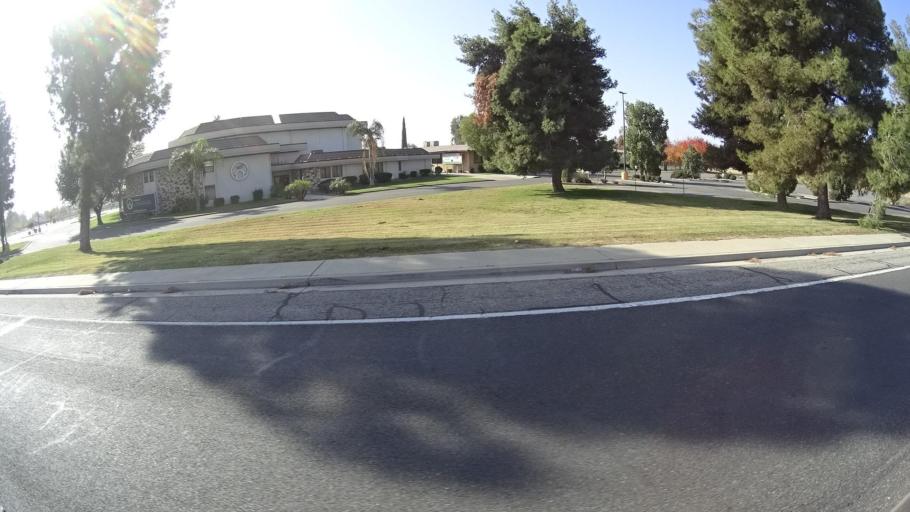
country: US
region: California
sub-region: Kern County
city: Oildale
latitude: 35.4382
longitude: -119.0142
